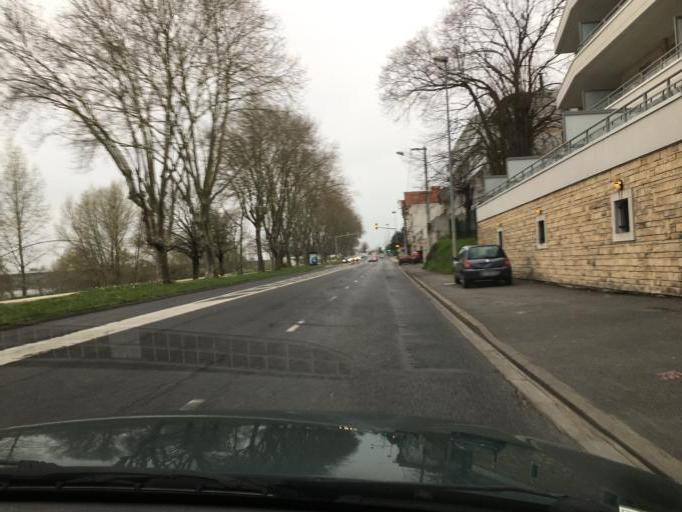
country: FR
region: Centre
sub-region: Departement du Loiret
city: Saint-Pryve-Saint-Mesmin
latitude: 47.8980
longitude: 1.8822
